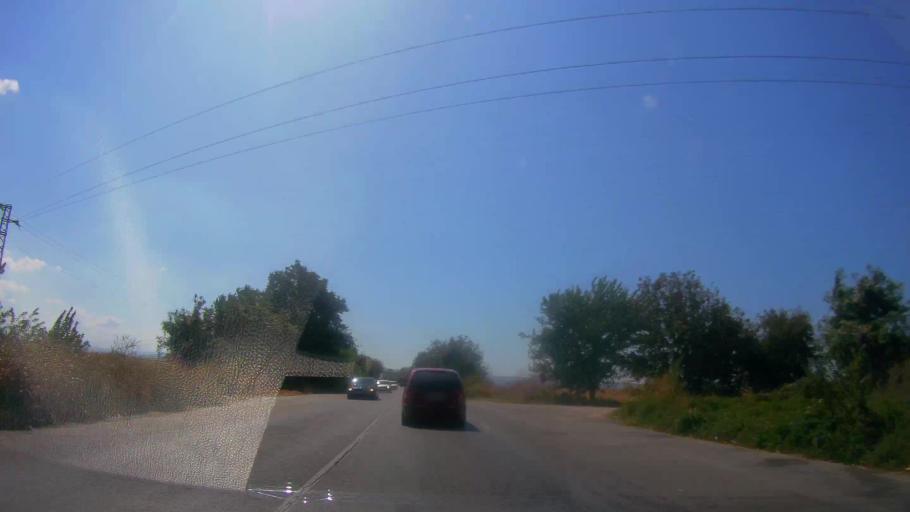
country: BG
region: Veliko Turnovo
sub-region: Obshtina Gorna Oryakhovitsa
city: Purvomaytsi
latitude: 43.2361
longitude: 25.6407
